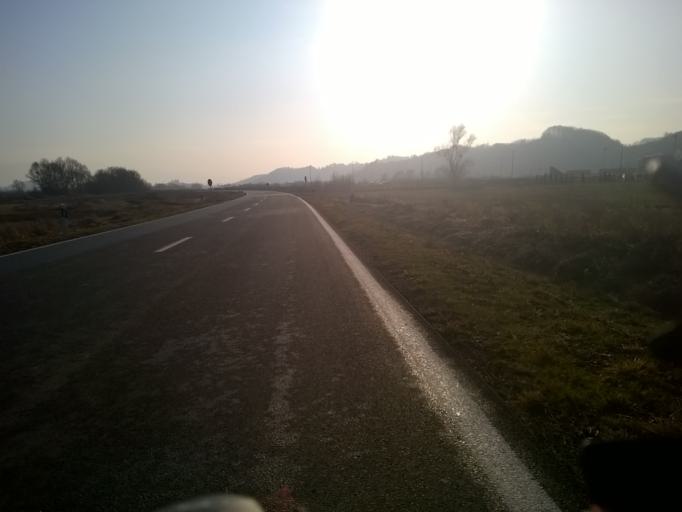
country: HR
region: Krapinsko-Zagorska
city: Zabok
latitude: 46.0690
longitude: 15.9138
